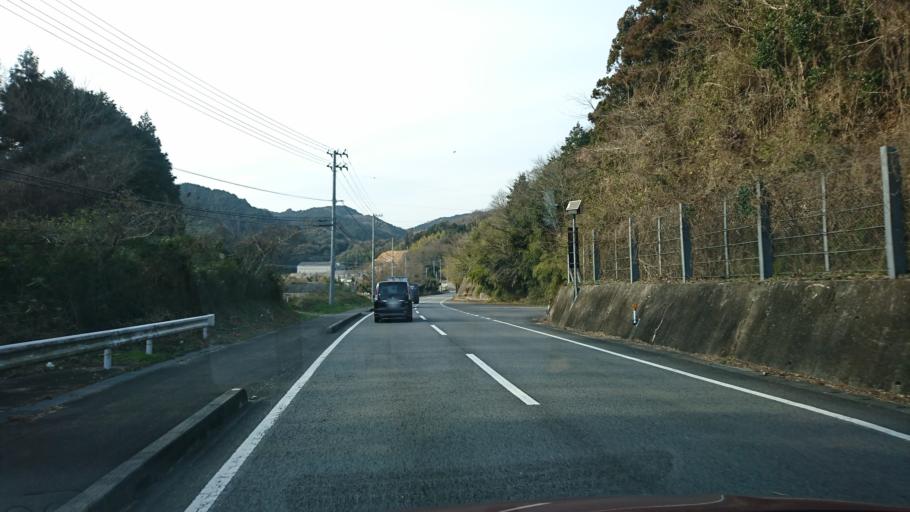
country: JP
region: Ehime
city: Hojo
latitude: 33.9950
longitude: 132.9264
